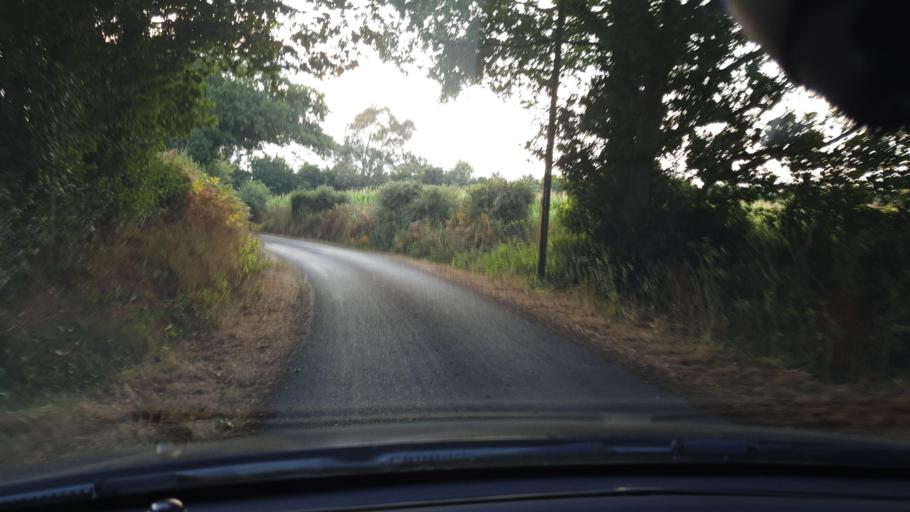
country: GB
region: England
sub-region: Essex
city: Alresford
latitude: 51.9079
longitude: 1.0166
